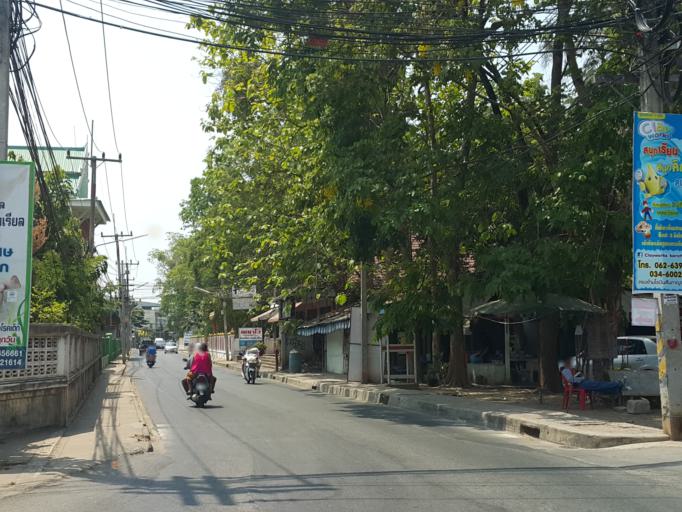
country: TH
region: Kanchanaburi
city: Kanchanaburi
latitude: 14.0290
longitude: 99.5262
